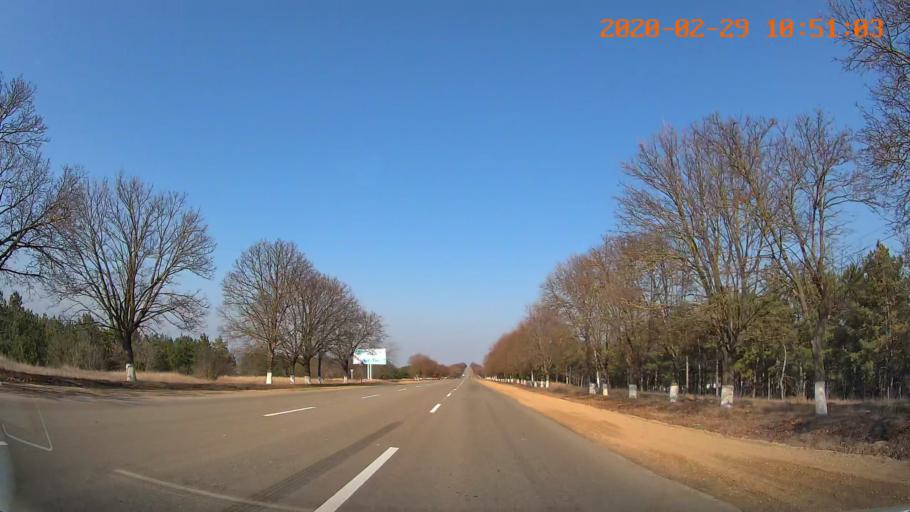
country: MD
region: Telenesti
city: Grigoriopol
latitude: 47.0892
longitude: 29.3692
